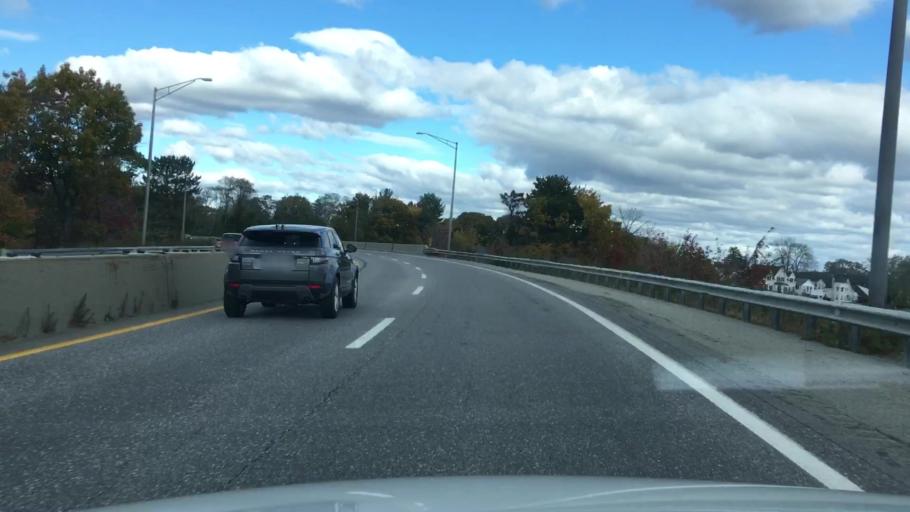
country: US
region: Maine
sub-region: Cumberland County
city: Portland
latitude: 43.6846
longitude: -70.2521
